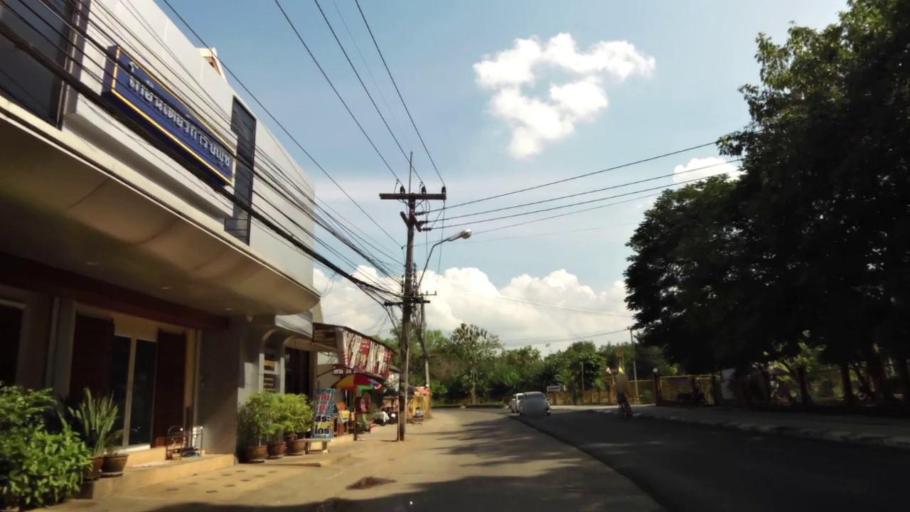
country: TH
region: Phrae
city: Phrae
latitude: 18.1345
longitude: 100.1375
